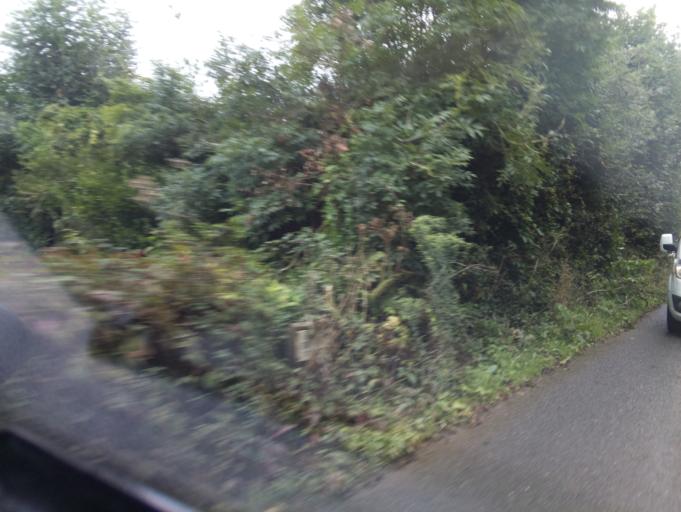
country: GB
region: England
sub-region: Devon
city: Kingsbridge
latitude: 50.2690
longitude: -3.8241
